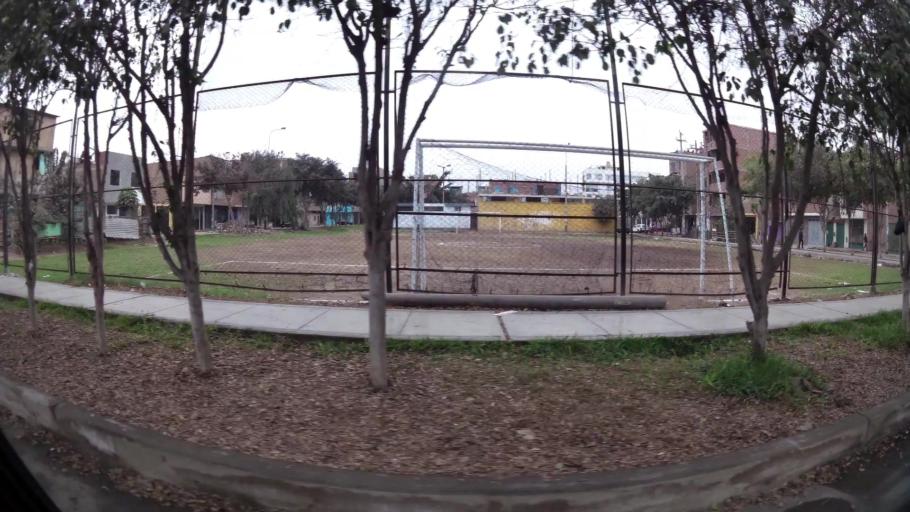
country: PE
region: Lima
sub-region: Lima
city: Independencia
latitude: -11.9561
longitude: -77.0794
